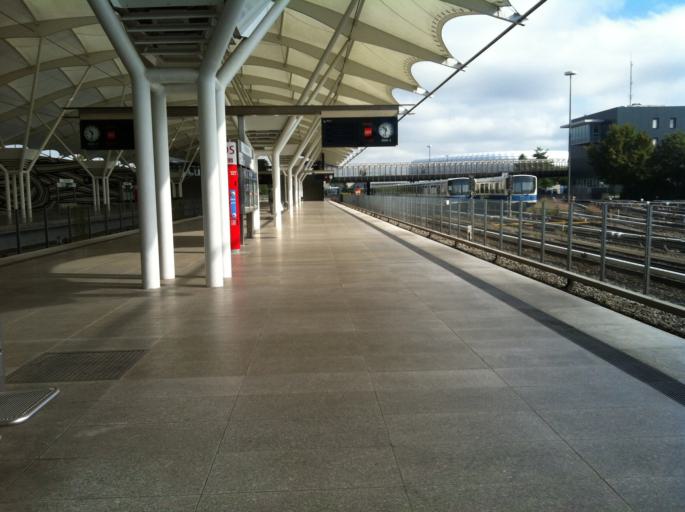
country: DE
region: Bavaria
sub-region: Upper Bavaria
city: Unterfoehring
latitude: 48.2114
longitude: 11.6166
